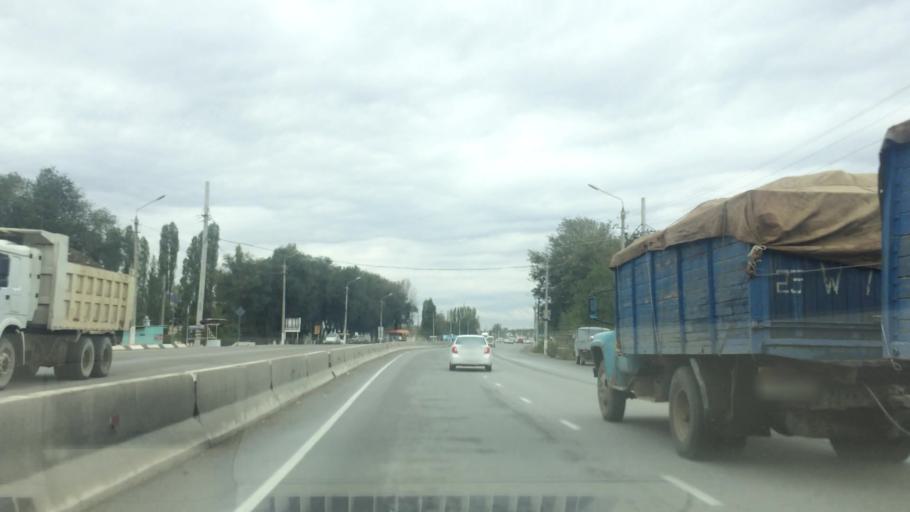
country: UZ
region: Jizzax
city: Jizzax
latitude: 39.9855
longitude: 67.5755
